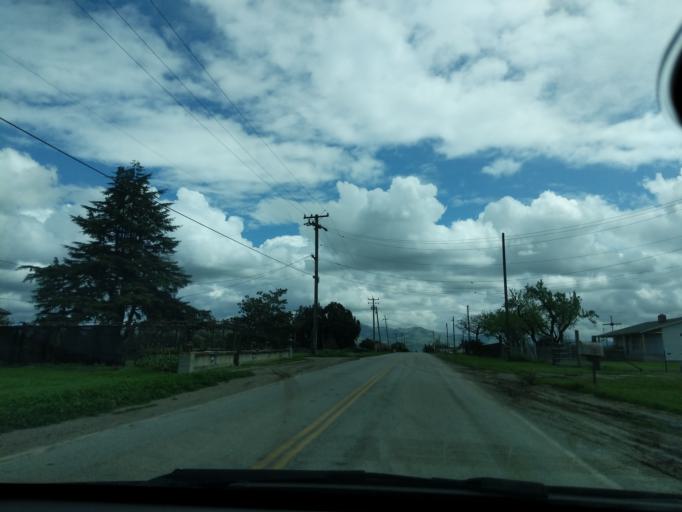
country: US
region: California
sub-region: San Benito County
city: Hollister
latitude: 36.8702
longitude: -121.4229
